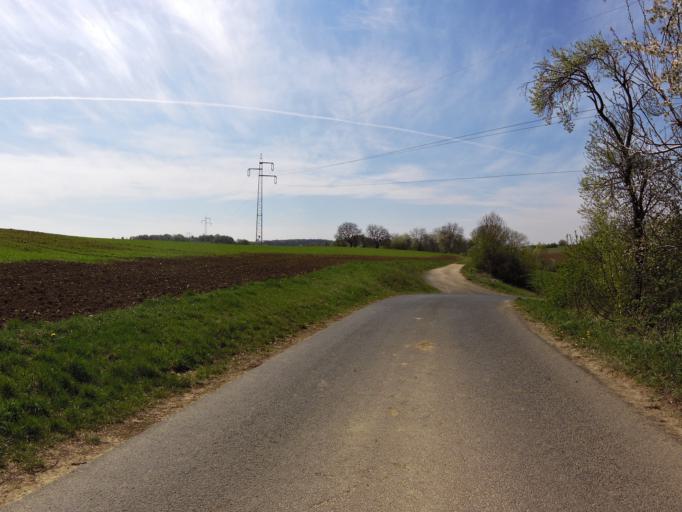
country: DE
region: Bavaria
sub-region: Regierungsbezirk Unterfranken
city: Kurnach
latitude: 49.8624
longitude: 10.0289
